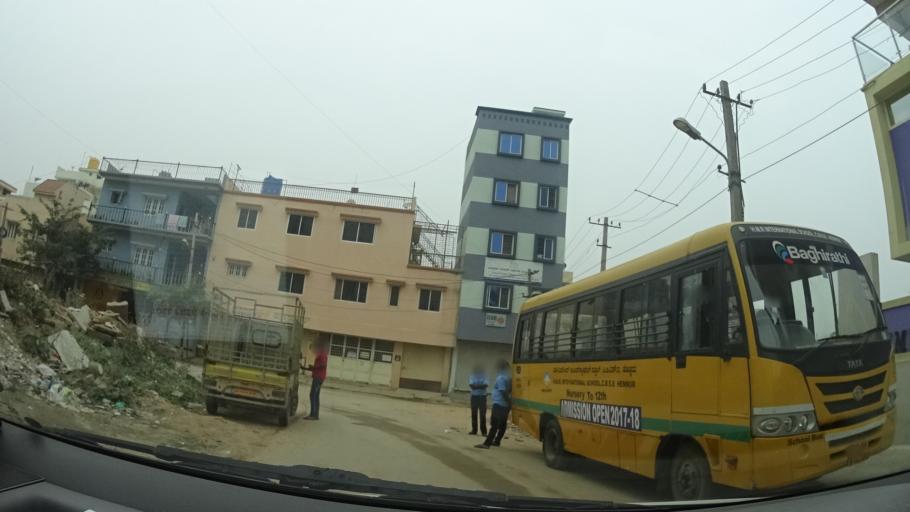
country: IN
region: Karnataka
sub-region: Bangalore Urban
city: Bangalore
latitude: 13.0335
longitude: 77.6336
